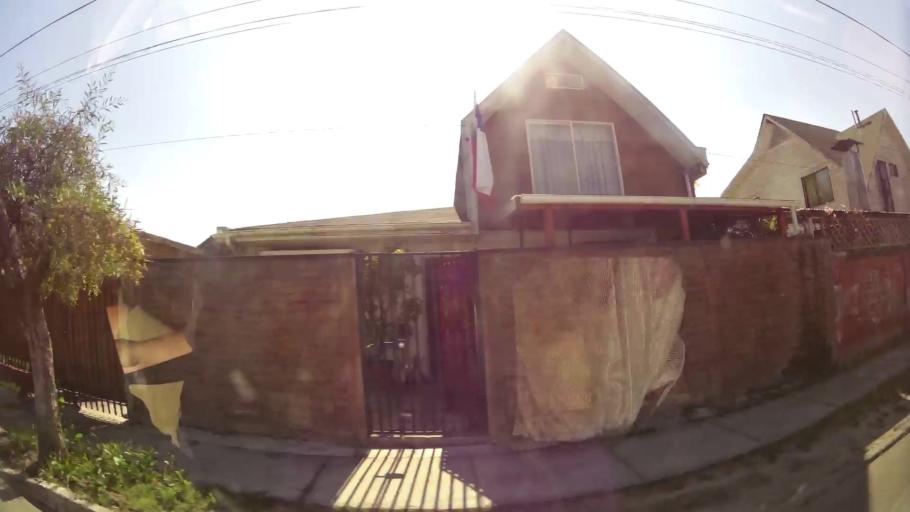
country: CL
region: Santiago Metropolitan
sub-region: Provincia de Talagante
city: Penaflor
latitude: -33.5673
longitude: -70.8050
